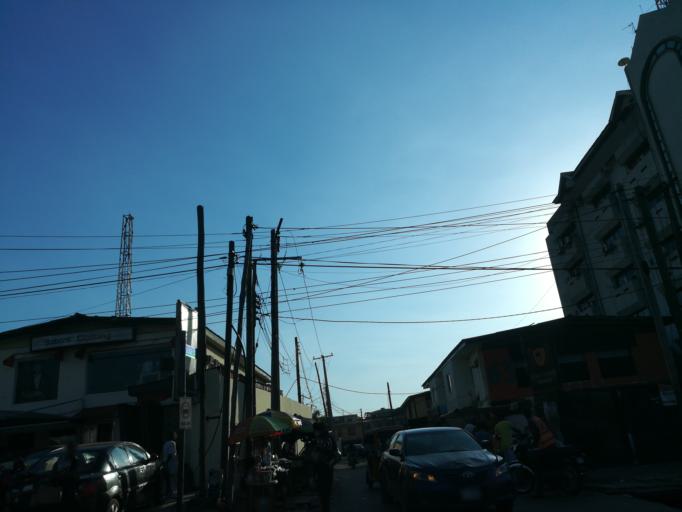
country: NG
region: Lagos
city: Ikeja
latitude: 6.6023
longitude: 3.3516
